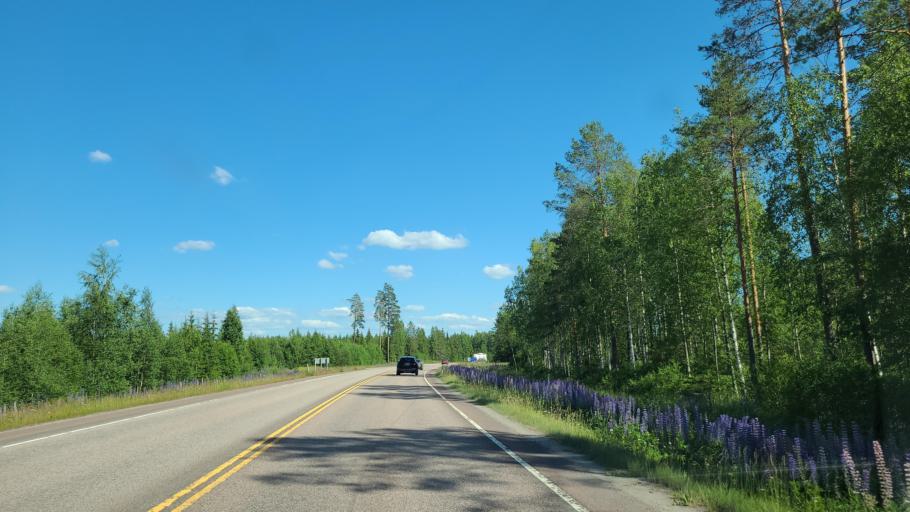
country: FI
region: Central Finland
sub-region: Jyvaeskylae
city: Petaejaevesi
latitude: 62.2714
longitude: 25.4155
